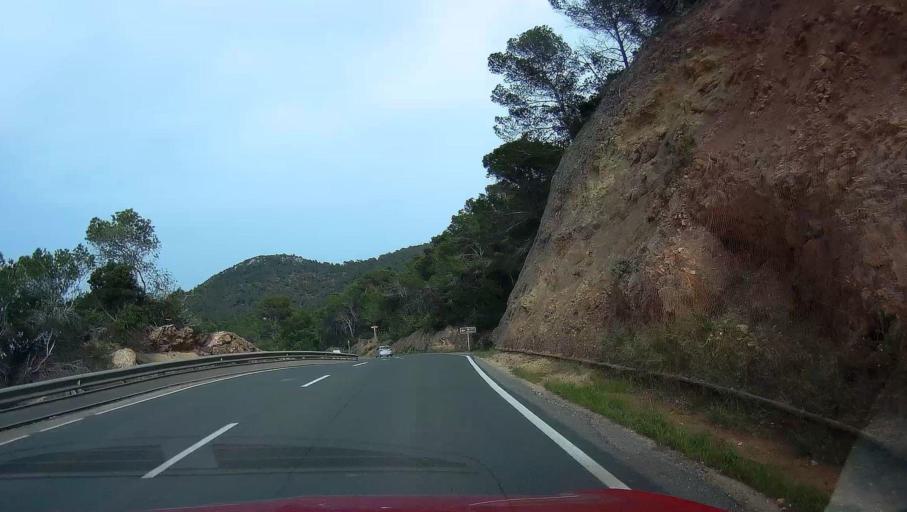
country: ES
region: Balearic Islands
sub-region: Illes Balears
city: Sant Joan de Labritja
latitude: 39.0995
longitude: 1.5021
